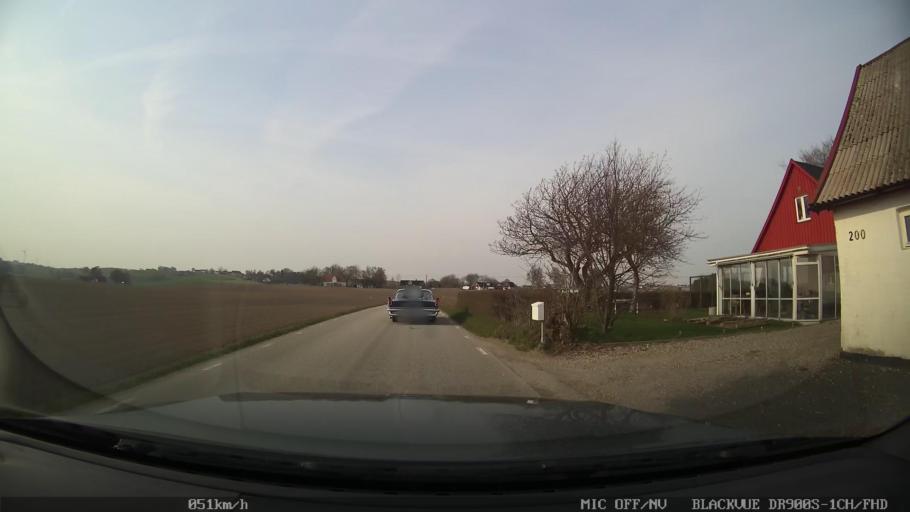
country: SE
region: Skane
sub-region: Ystads Kommun
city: Ystad
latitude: 55.4610
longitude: 13.8253
